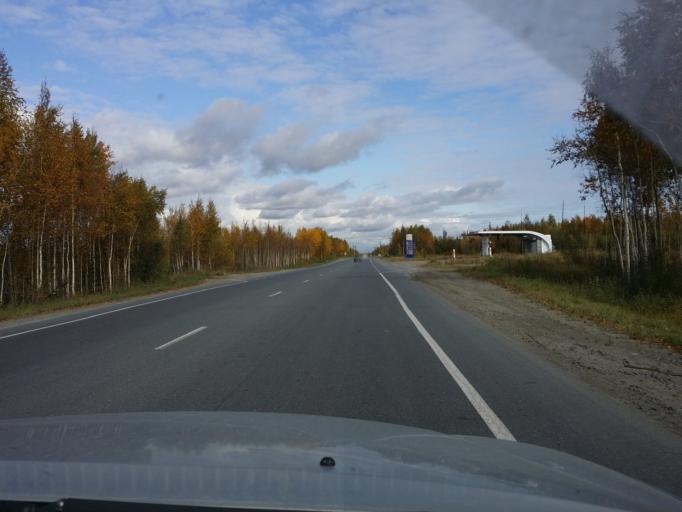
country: RU
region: Khanty-Mansiyskiy Avtonomnyy Okrug
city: Megion
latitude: 61.0678
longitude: 76.1156
